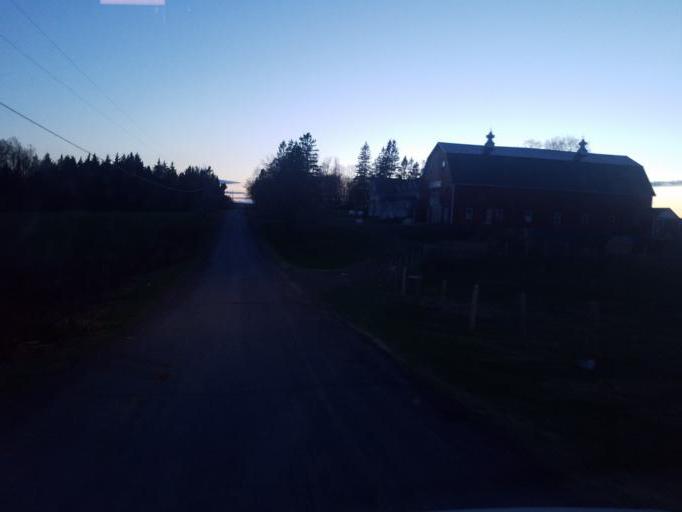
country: US
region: Maine
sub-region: Aroostook County
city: Caribou
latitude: 46.8673
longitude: -68.1998
